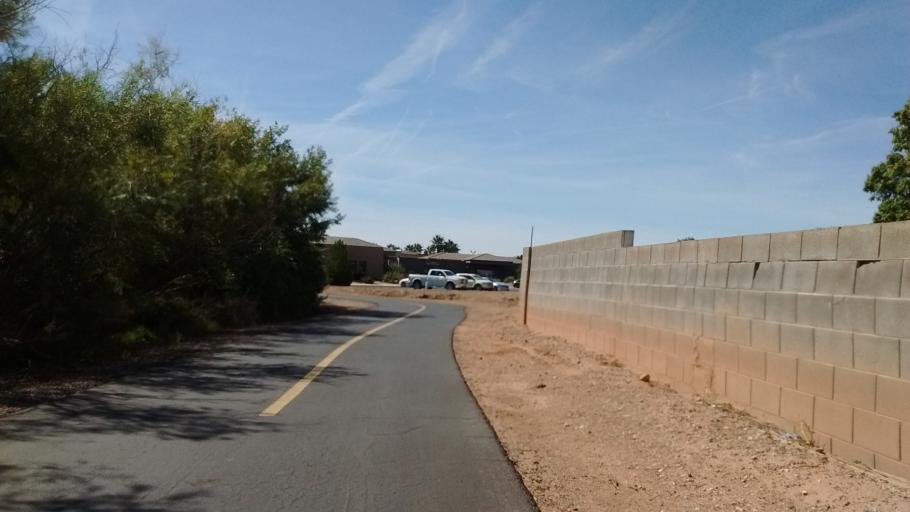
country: US
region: Utah
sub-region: Washington County
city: Saint George
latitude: 37.0835
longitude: -113.5734
